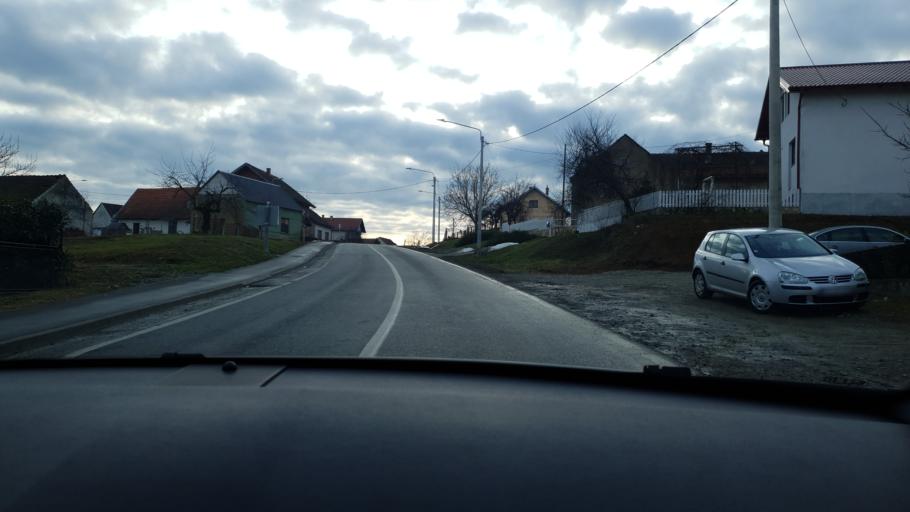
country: HR
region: Pozesko-Slavonska
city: Vidovci
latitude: 45.3543
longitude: 17.7260
